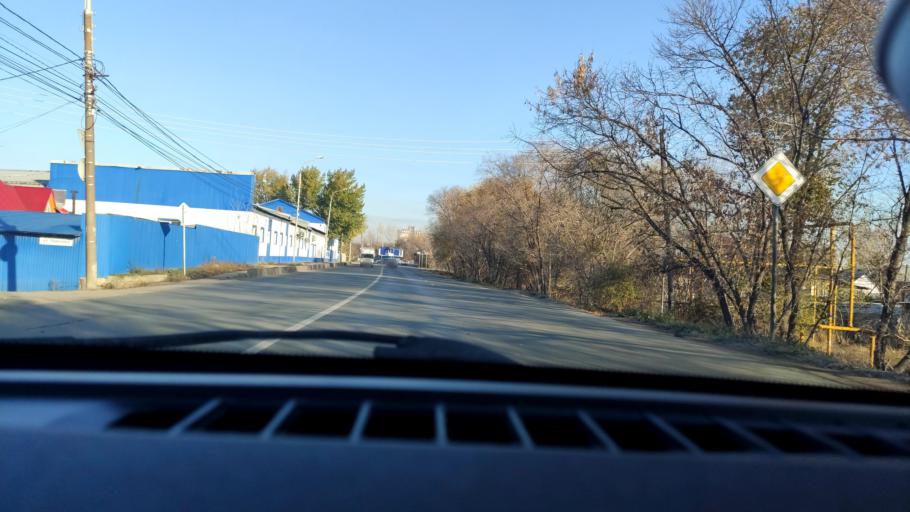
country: RU
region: Samara
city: Rozhdestveno
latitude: 53.1628
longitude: 50.0762
